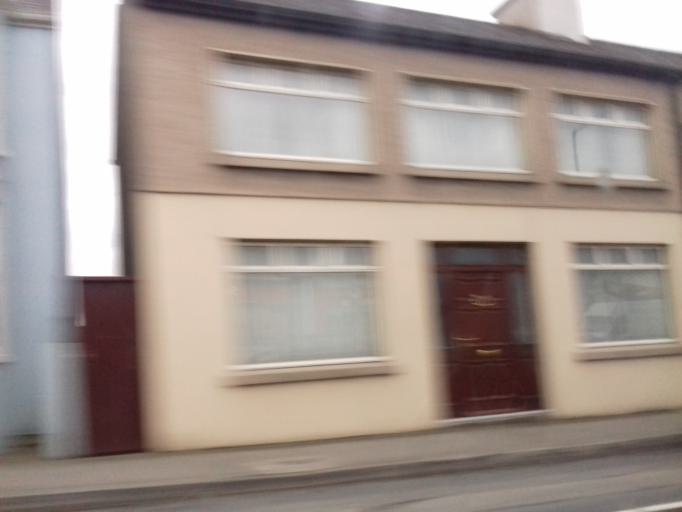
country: IE
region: Munster
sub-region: County Limerick
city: Abbeyfeale
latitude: 52.3828
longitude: -9.3016
